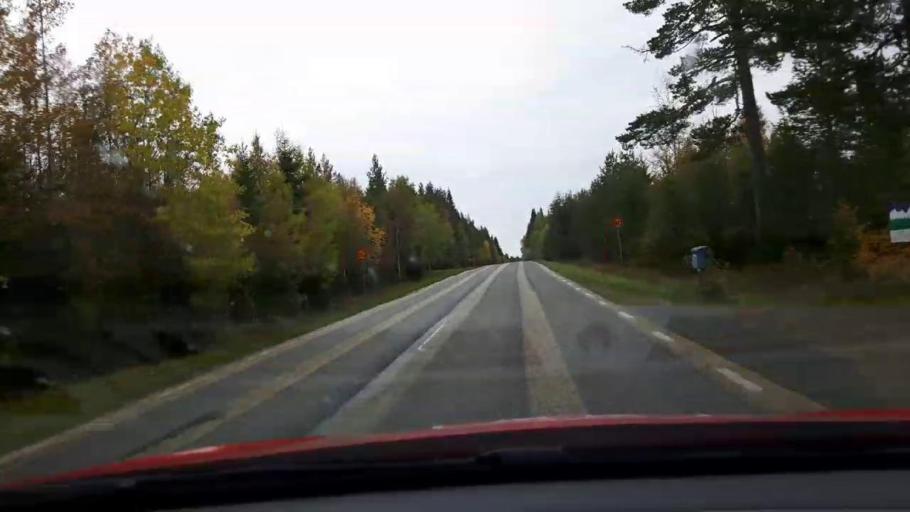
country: SE
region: Jaemtland
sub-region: Bergs Kommun
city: Hoverberg
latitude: 62.8965
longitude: 14.3472
